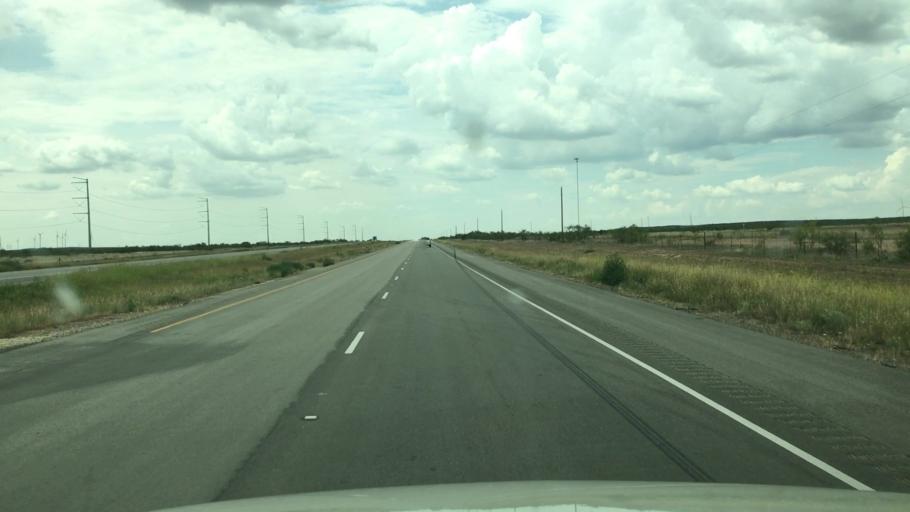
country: US
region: Texas
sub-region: Glasscock County
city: Garden City
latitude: 31.9742
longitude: -101.2463
